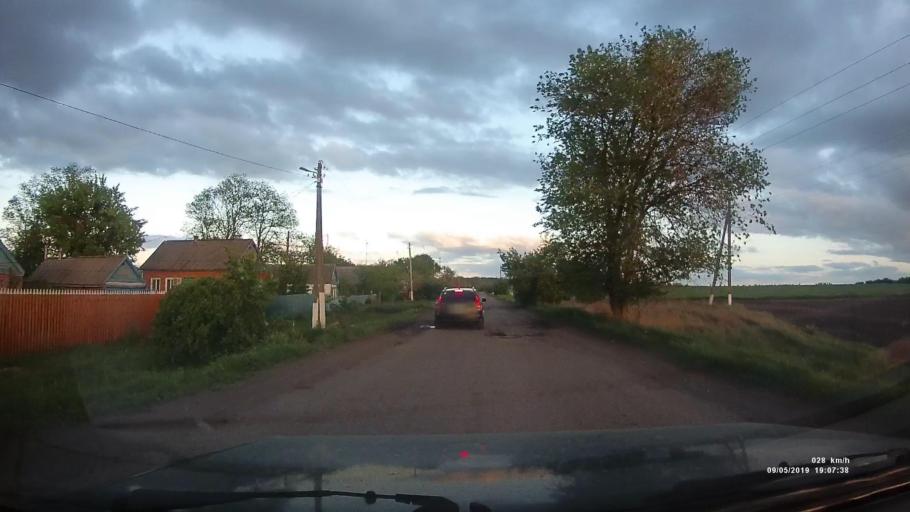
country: RU
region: Krasnodarskiy
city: Kanelovskaya
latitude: 46.7334
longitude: 39.1983
